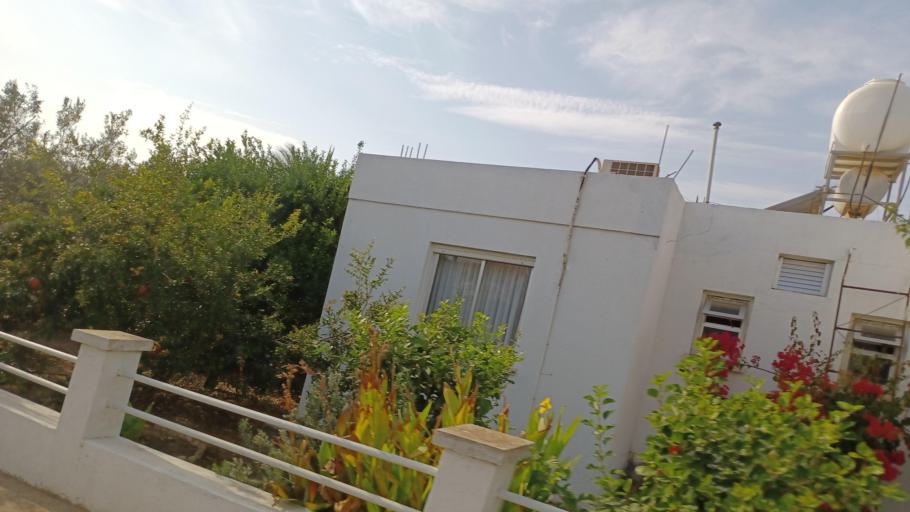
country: CY
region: Ammochostos
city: Paralimni
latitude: 35.0287
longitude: 33.9735
